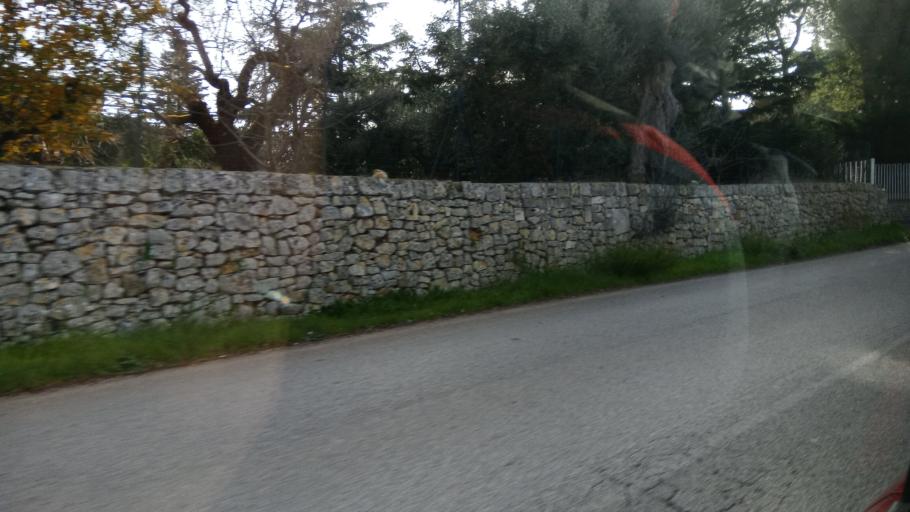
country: IT
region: Apulia
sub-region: Provincia di Bari
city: Castellana
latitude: 40.8977
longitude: 17.1660
